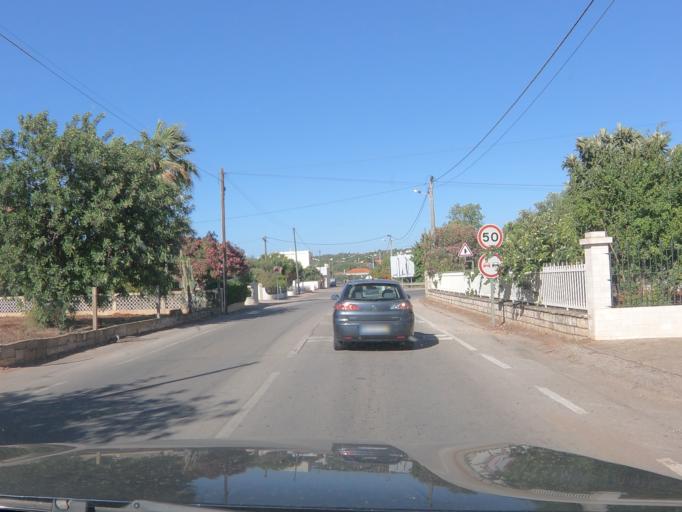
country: PT
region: Faro
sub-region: Loule
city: Almancil
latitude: 37.1029
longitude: -8.0573
